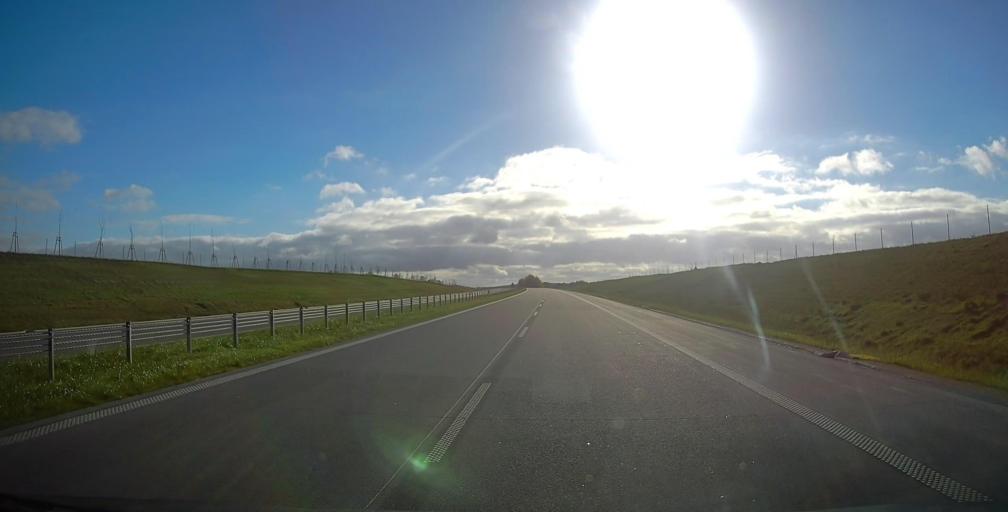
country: PL
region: Warmian-Masurian Voivodeship
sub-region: Powiat elcki
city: Elk
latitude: 53.7248
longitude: 22.2820
